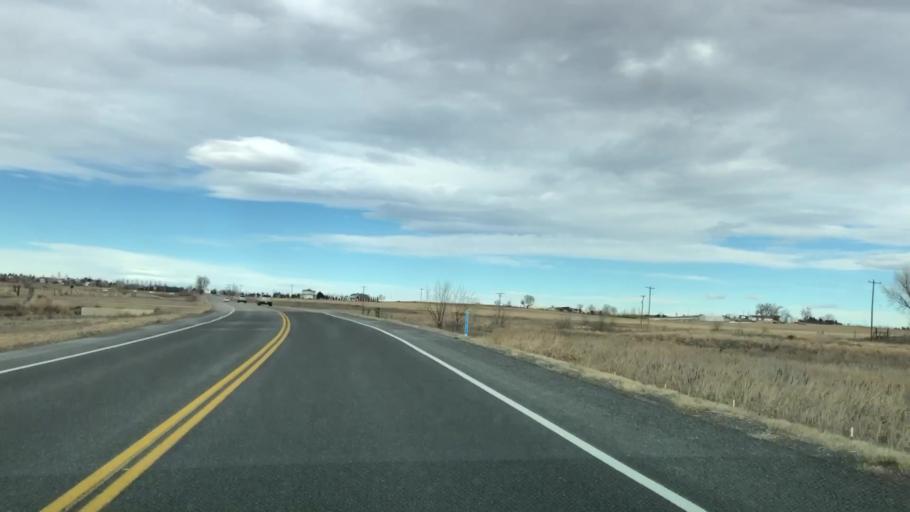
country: US
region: Colorado
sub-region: Weld County
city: Windsor
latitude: 40.5149
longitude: -104.9268
